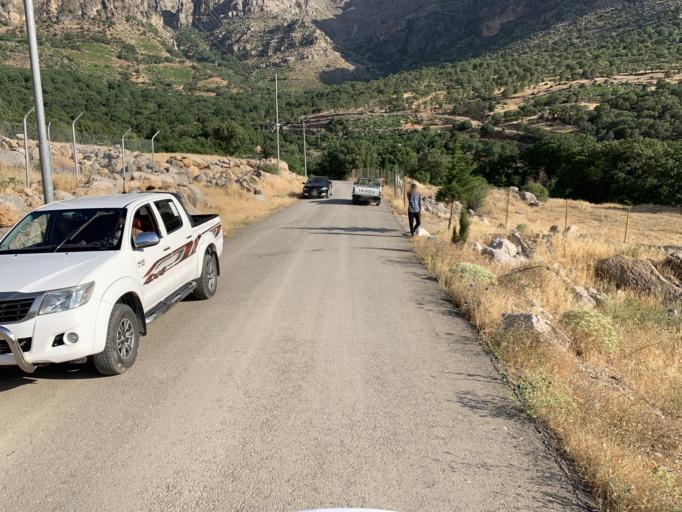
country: IQ
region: As Sulaymaniyah
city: Qeladize
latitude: 35.9902
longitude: 45.1999
